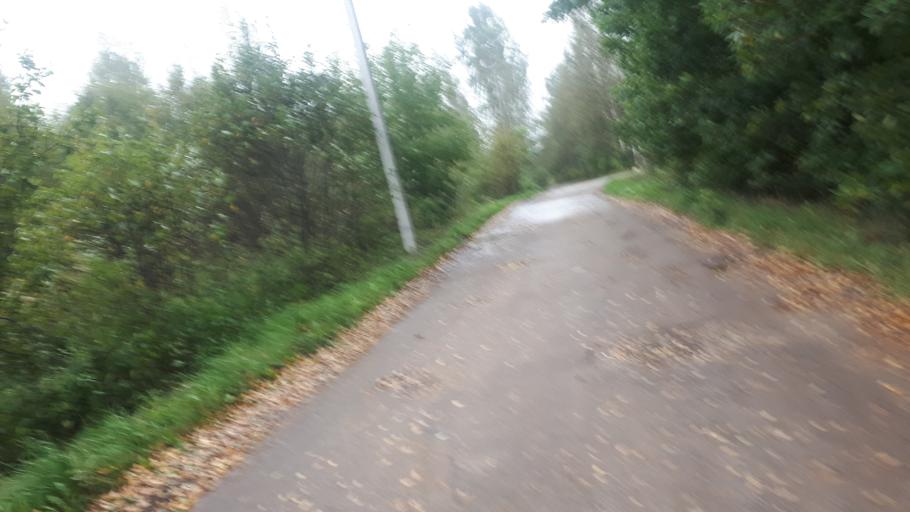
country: RU
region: Jaroslavl
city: Konstantinovskiy
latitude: 57.8263
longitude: 39.5853
